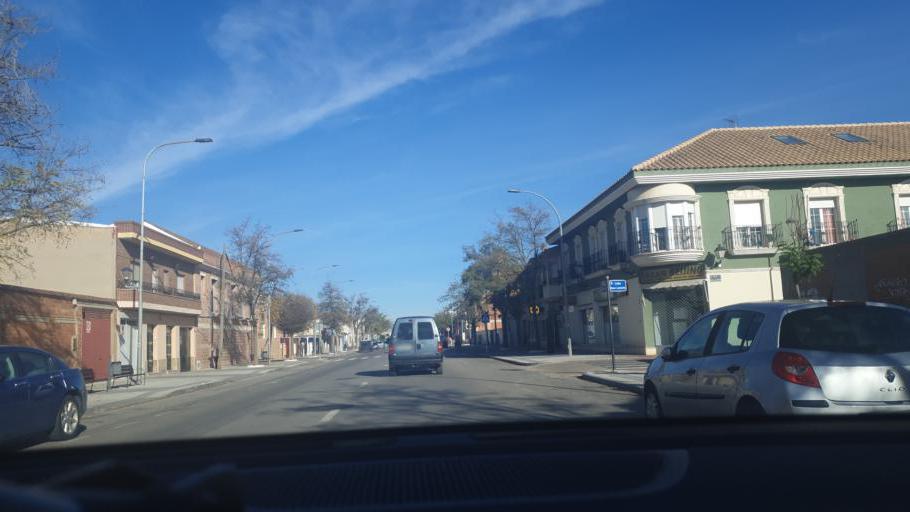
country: ES
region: Castille-La Mancha
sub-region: Provincia de Ciudad Real
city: Tomelloso
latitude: 39.1539
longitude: -3.0095
